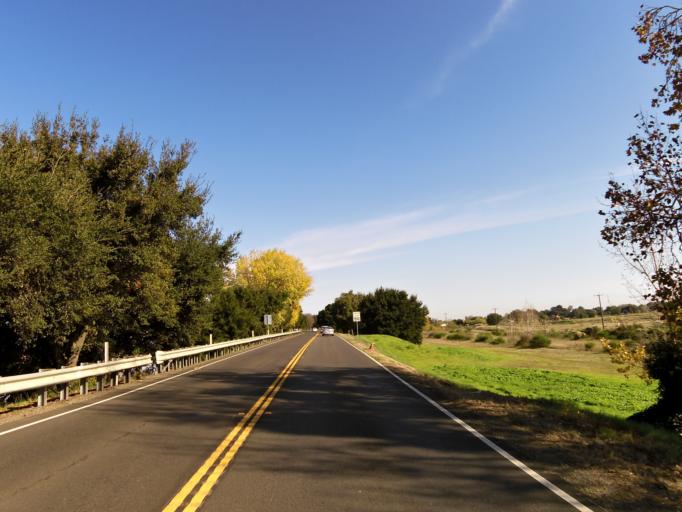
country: US
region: California
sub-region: Solano County
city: Rio Vista
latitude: 38.1643
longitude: -121.6022
